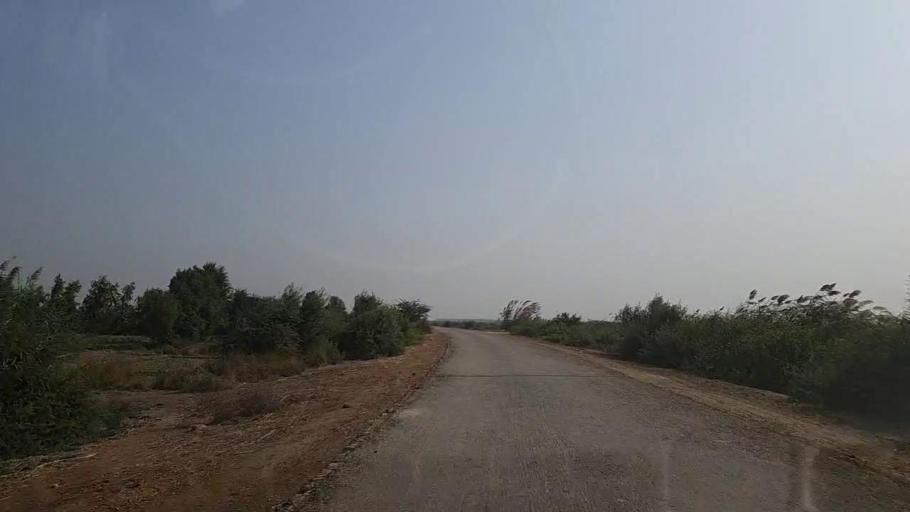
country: PK
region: Sindh
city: Keti Bandar
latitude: 24.2342
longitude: 67.6432
